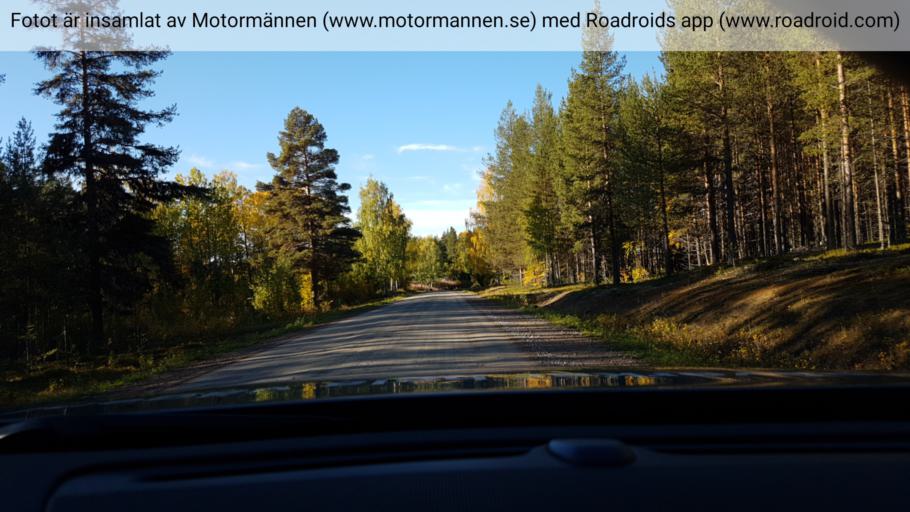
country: SE
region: Norrbotten
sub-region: Alvsbyns Kommun
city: AElvsbyn
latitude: 66.2656
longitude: 21.0830
